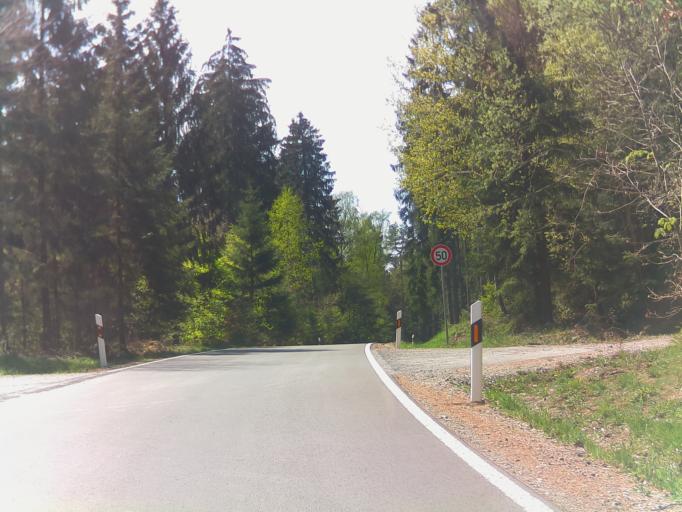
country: DE
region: Thuringia
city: Hildburghausen
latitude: 50.4494
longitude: 10.7708
